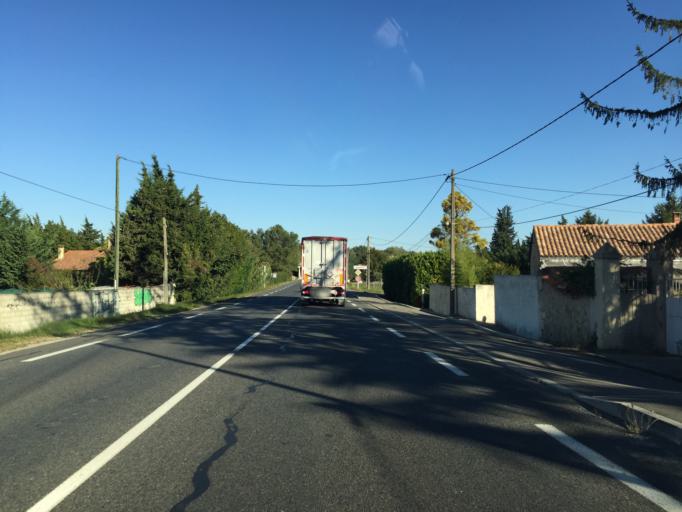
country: FR
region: Provence-Alpes-Cote d'Azur
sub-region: Departement du Vaucluse
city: Mondragon
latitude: 44.2468
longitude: 4.7113
